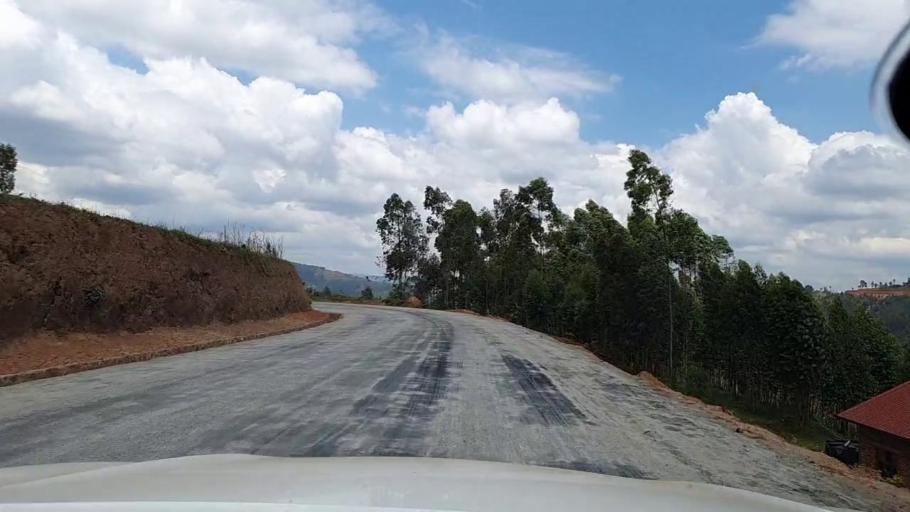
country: RW
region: Southern Province
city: Butare
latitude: -2.6984
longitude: 29.5676
